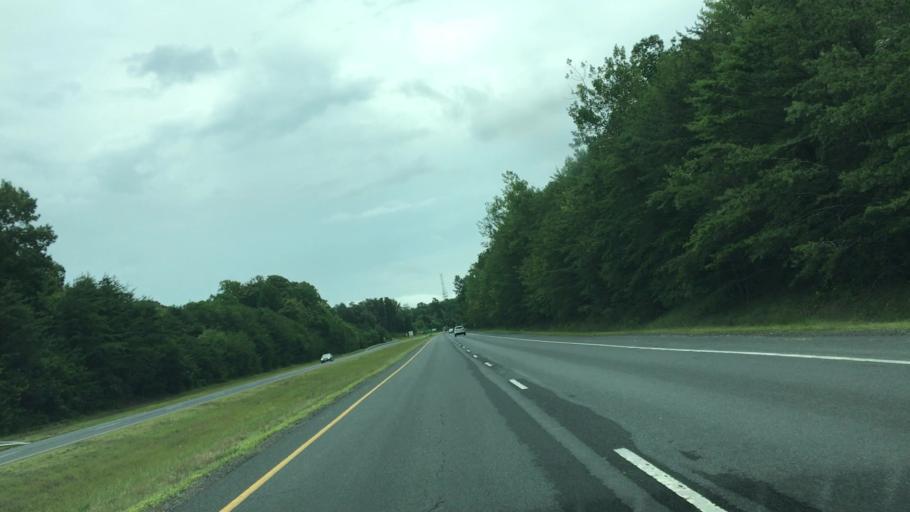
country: US
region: Virginia
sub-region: Prince William County
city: Lake Ridge
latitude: 38.6827
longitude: -77.3680
